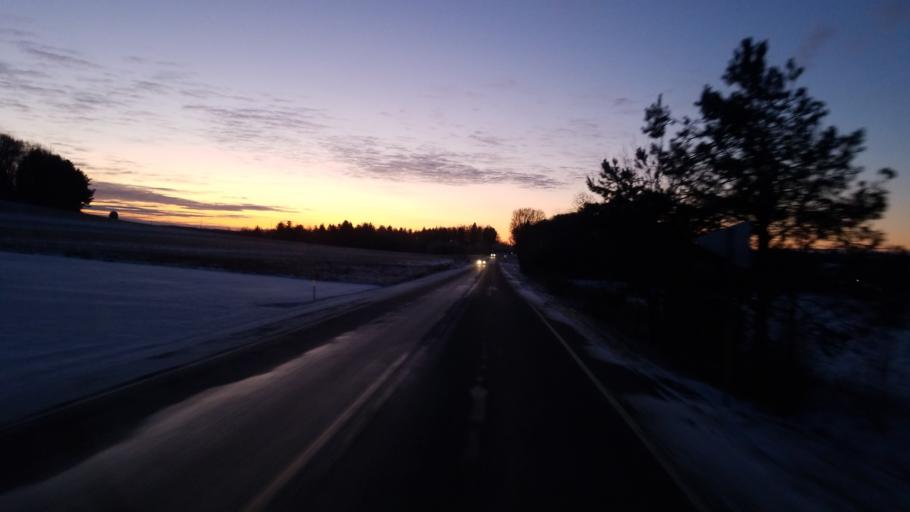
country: US
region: Pennsylvania
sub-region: Clarion County
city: Knox
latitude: 41.2590
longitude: -79.5553
